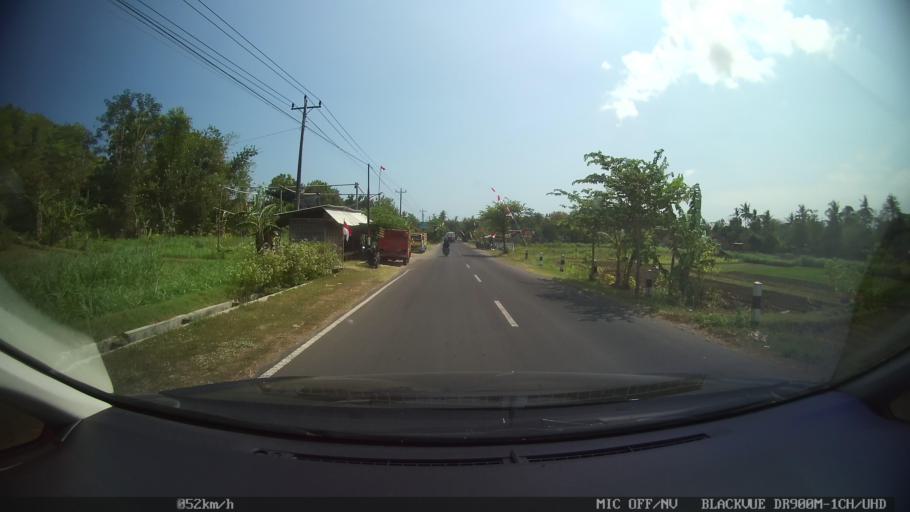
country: ID
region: Daerah Istimewa Yogyakarta
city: Pundong
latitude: -7.9875
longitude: 110.3230
